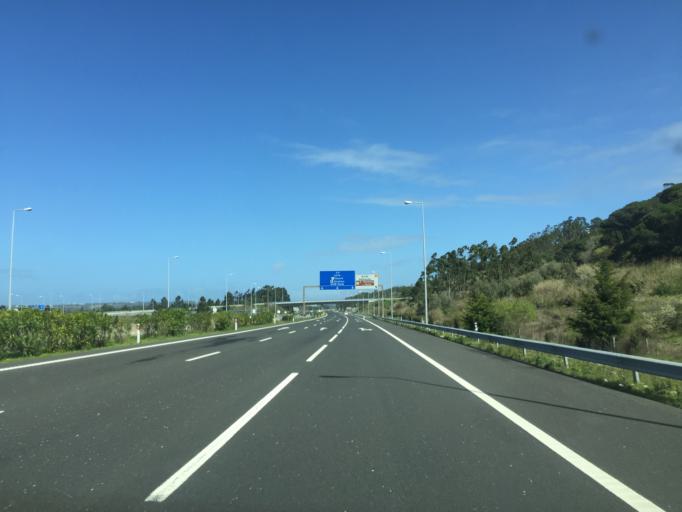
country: PT
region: Leiria
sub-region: Caldas da Rainha
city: Caldas da Rainha
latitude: 39.4986
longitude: -9.0913
